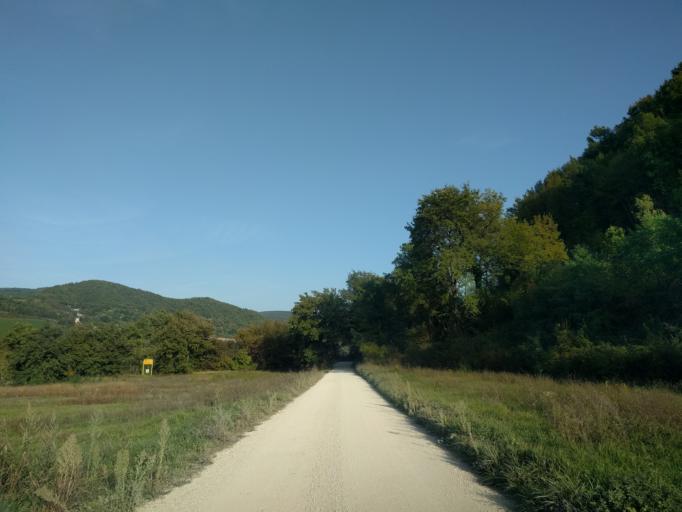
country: IT
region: The Marches
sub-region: Provincia di Pesaro e Urbino
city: Canavaccio
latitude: 43.6969
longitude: 12.6794
